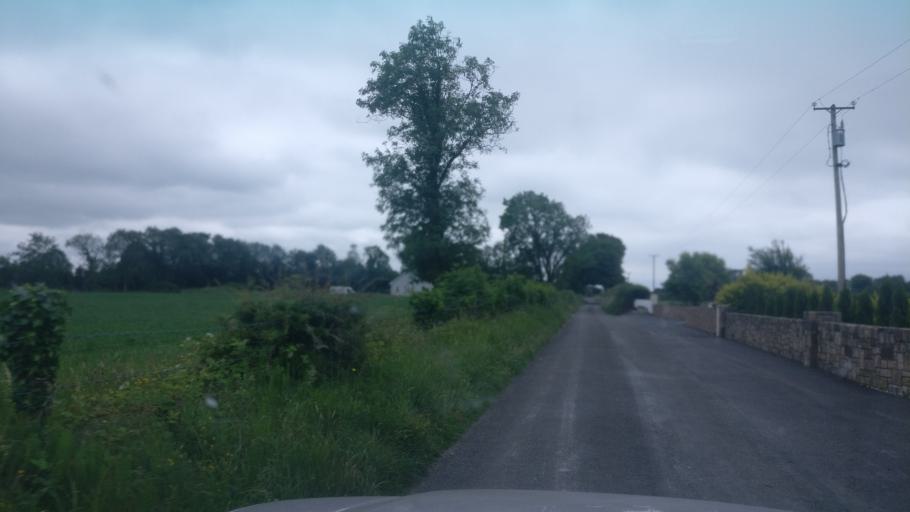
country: IE
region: Connaught
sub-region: County Galway
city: Ballinasloe
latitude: 53.2948
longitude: -8.3403
